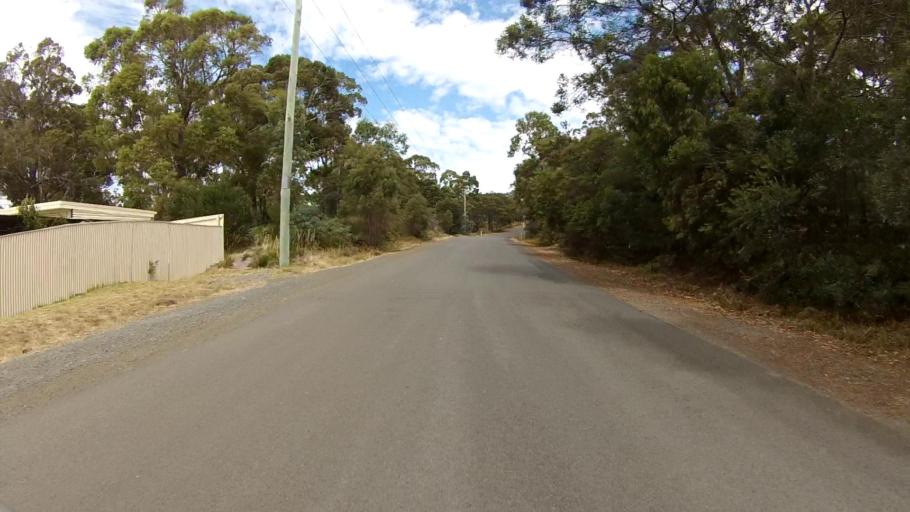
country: AU
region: Tasmania
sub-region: Sorell
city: Sorell
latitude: -42.8938
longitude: 147.6863
